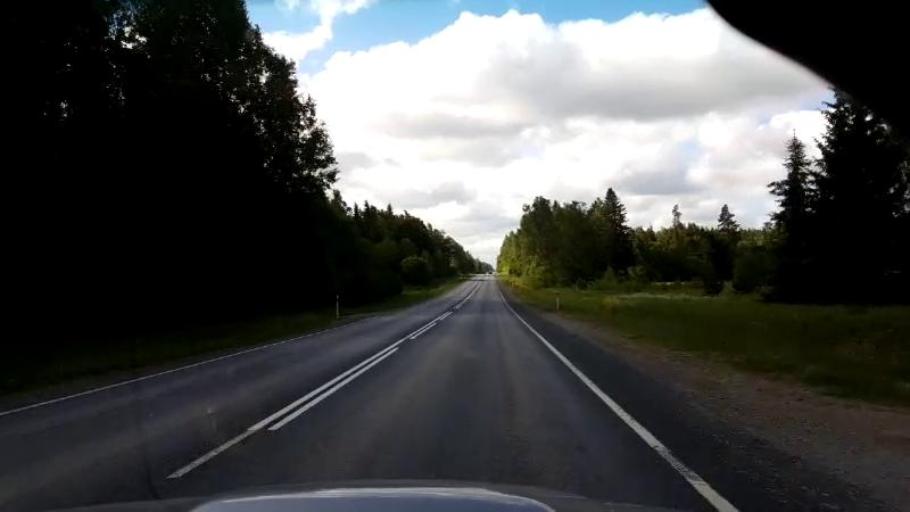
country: EE
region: Harju
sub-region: Saue linn
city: Saue
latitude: 59.2277
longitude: 24.4933
